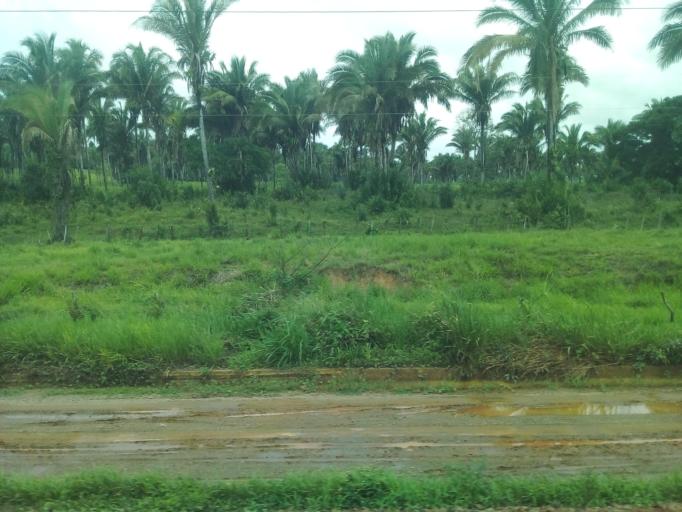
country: BR
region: Maranhao
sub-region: Vitoria Do Mearim
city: Vitoria do Mearim
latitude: -3.5323
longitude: -44.8654
